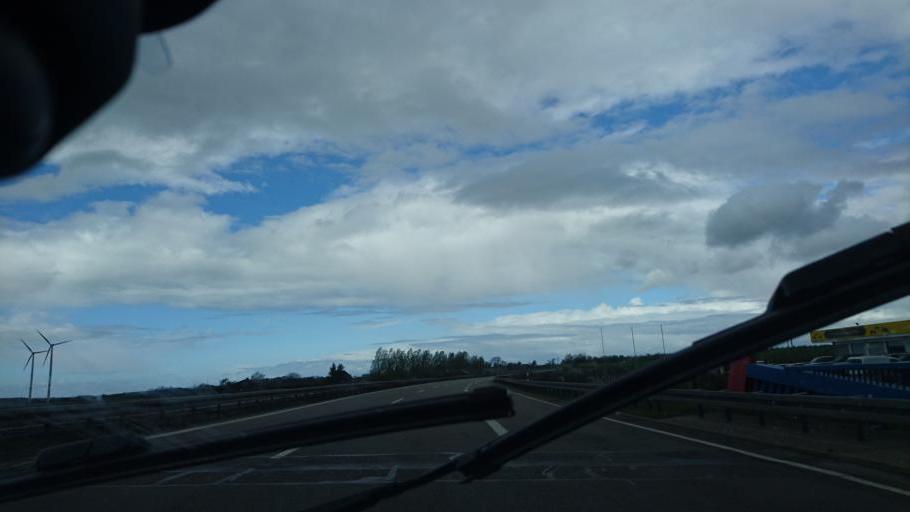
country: DE
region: Mecklenburg-Vorpommern
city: Stabelow
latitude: 54.0442
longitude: 12.0345
